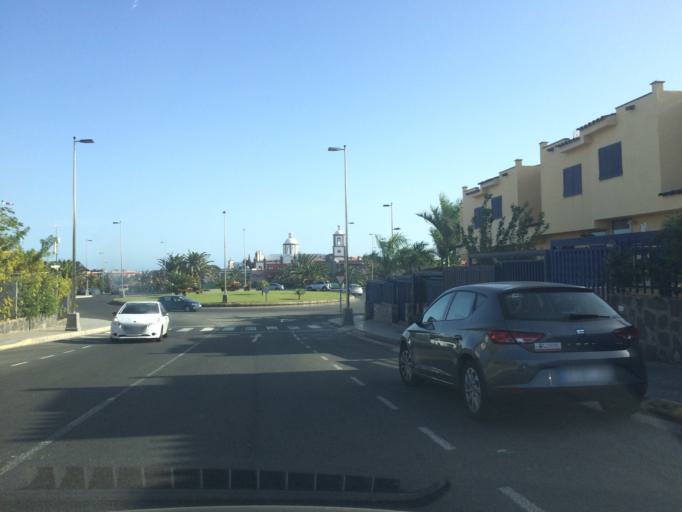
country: ES
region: Canary Islands
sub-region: Provincia de Las Palmas
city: Maspalomas
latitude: 27.7450
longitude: -15.6081
